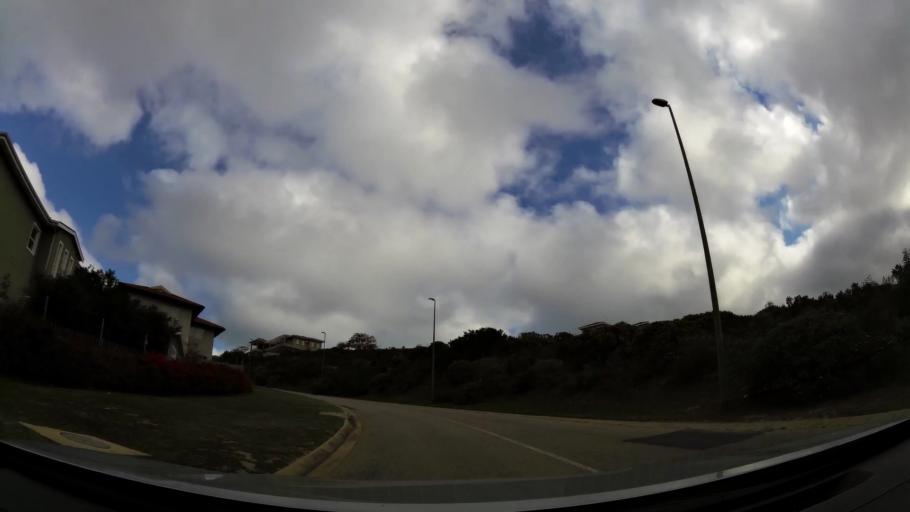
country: ZA
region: Western Cape
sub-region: Eden District Municipality
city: Plettenberg Bay
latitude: -34.0860
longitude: 23.3556
